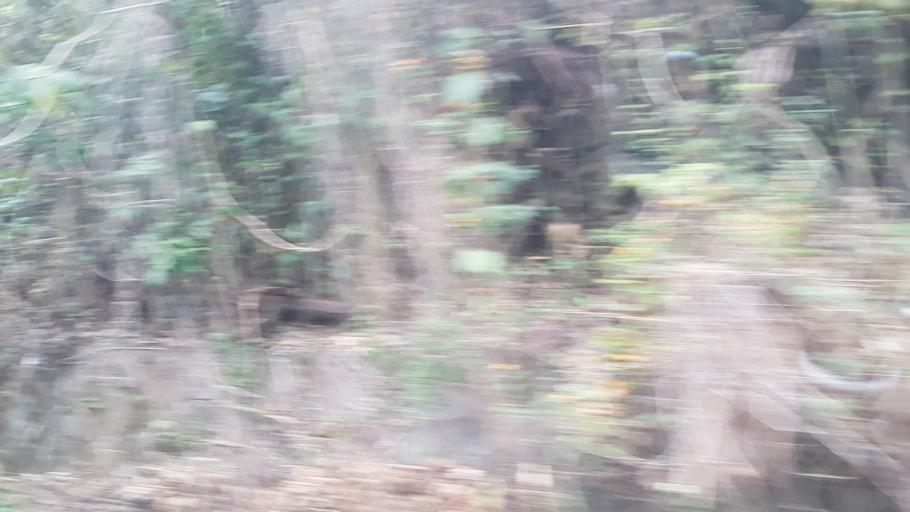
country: TW
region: Taiwan
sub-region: Chiayi
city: Jiayi Shi
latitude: 23.3260
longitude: 120.4887
